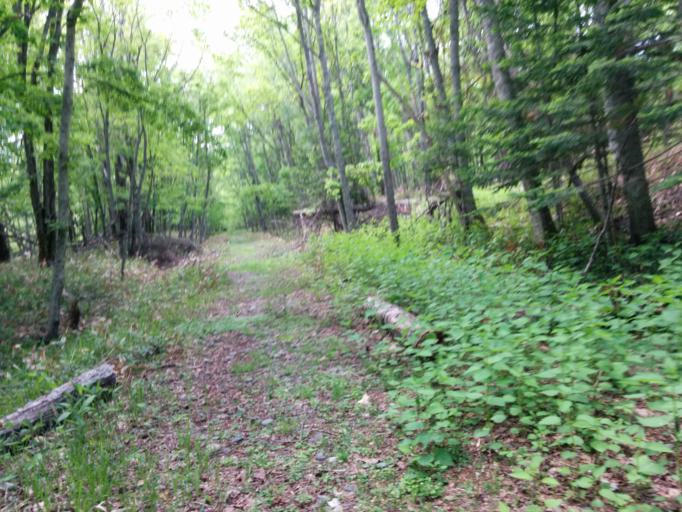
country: JP
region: Hokkaido
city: Otofuke
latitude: 43.3994
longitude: 143.1829
